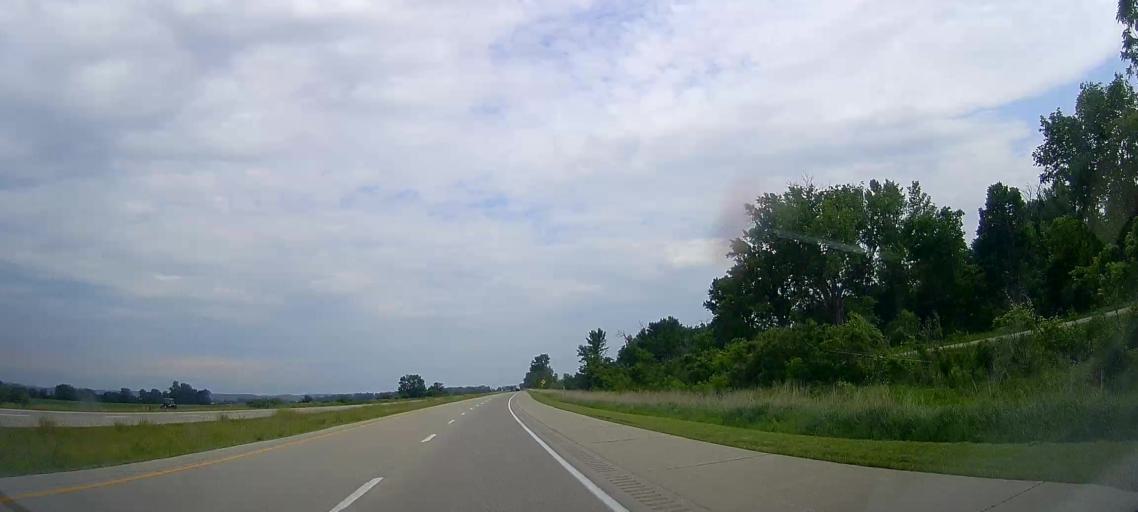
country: US
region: Nebraska
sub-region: Burt County
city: Tekamah
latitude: 41.8385
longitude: -96.0870
